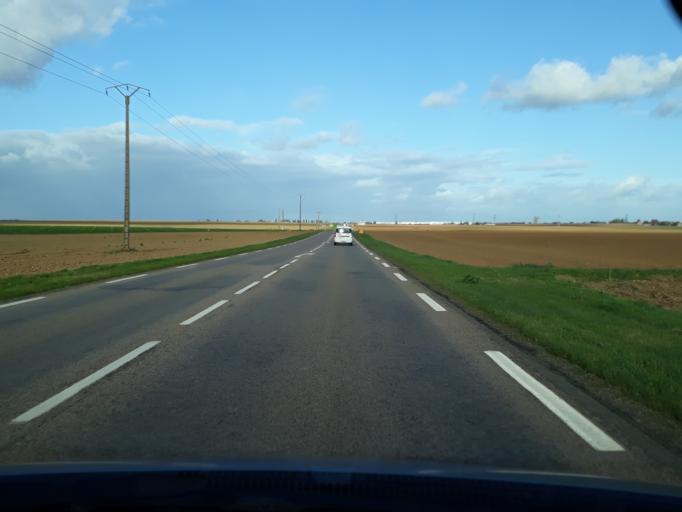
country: FR
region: Centre
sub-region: Departement du Loiret
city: Dadonville
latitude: 48.2276
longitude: 2.3162
